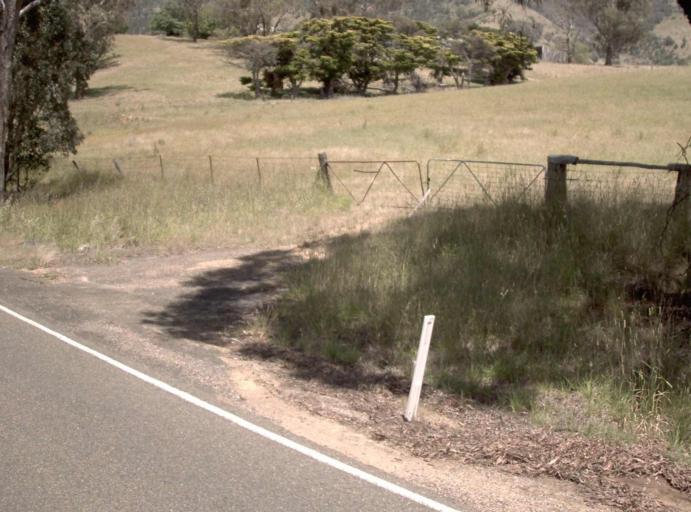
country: AU
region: Victoria
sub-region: East Gippsland
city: Bairnsdale
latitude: -37.4073
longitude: 147.8362
